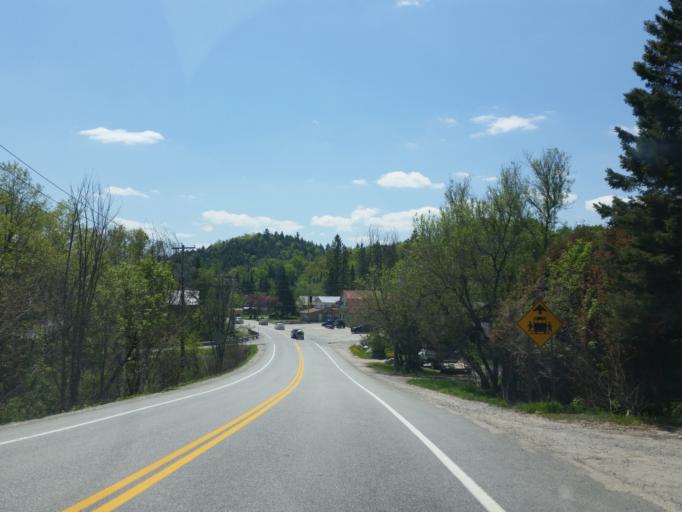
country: CA
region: Quebec
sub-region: Outaouais
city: Wakefield
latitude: 45.6842
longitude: -75.9308
